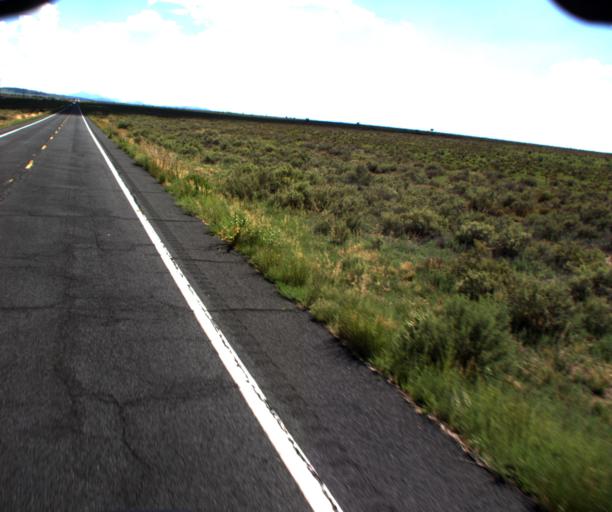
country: US
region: Arizona
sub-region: Coconino County
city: Williams
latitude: 35.6219
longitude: -112.1436
